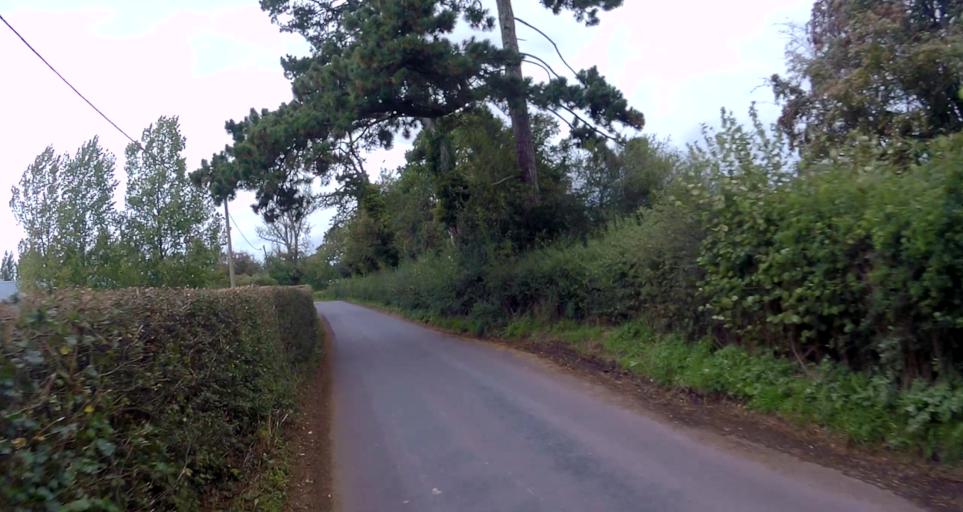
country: GB
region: England
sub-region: Hampshire
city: Four Marks
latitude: 51.1369
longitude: -1.0806
